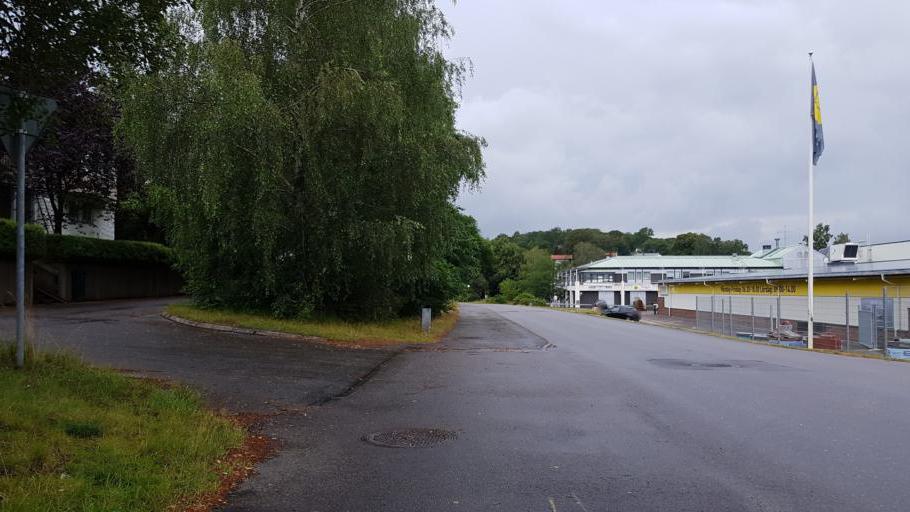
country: SE
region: Vaestra Goetaland
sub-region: Harryda Kommun
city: Molnlycke
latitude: 57.6551
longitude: 12.1152
